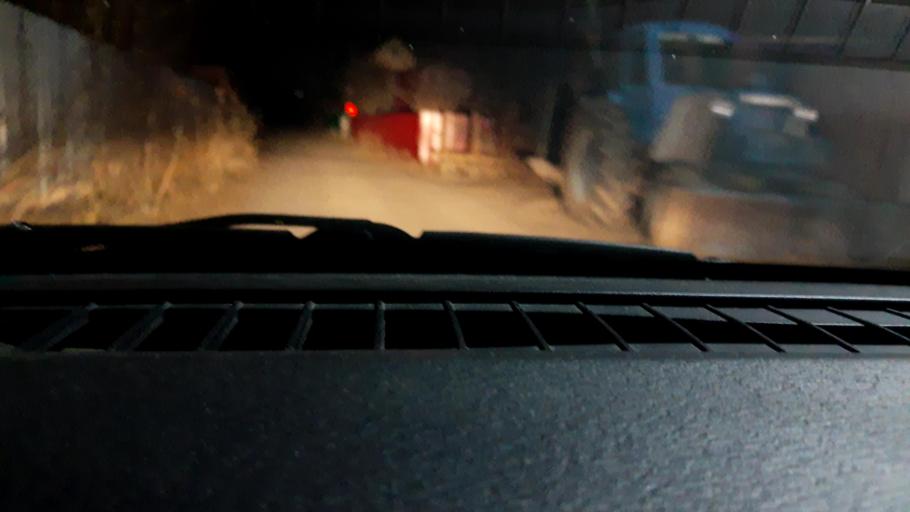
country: RU
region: Nizjnij Novgorod
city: Gorbatovka
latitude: 56.2557
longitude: 43.8016
